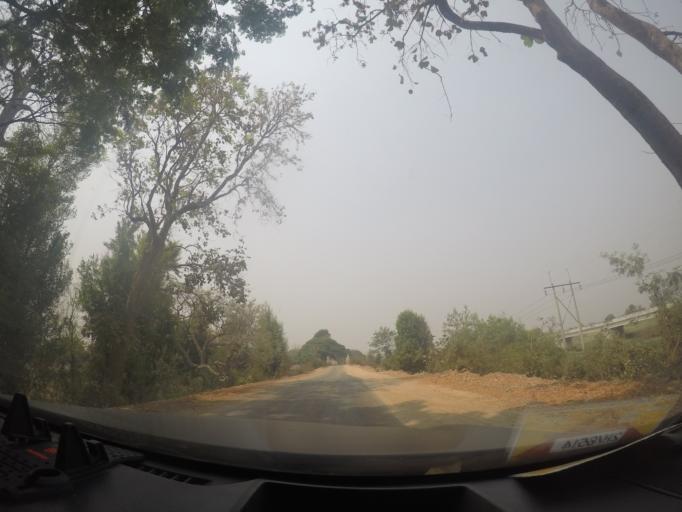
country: MM
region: Magway
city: Taungdwingyi
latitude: 19.8689
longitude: 95.5170
